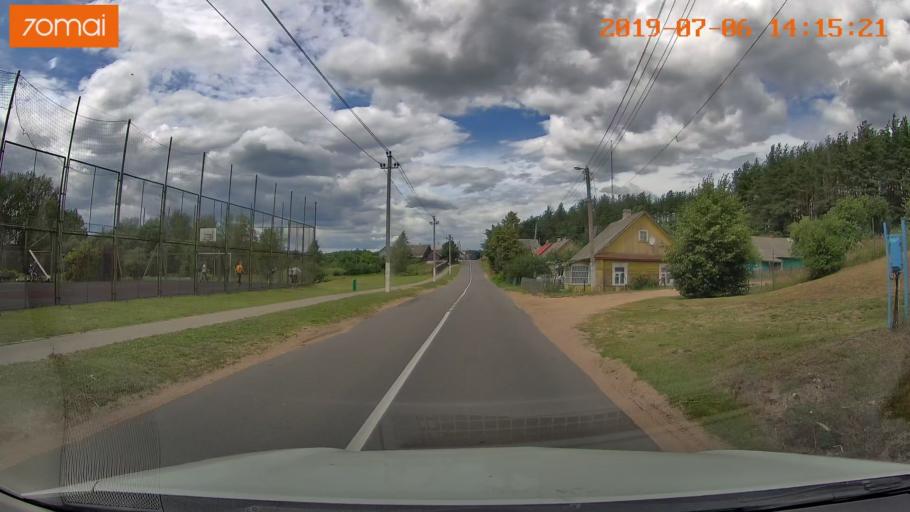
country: BY
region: Minsk
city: Ivyanyets
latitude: 53.8927
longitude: 26.7368
